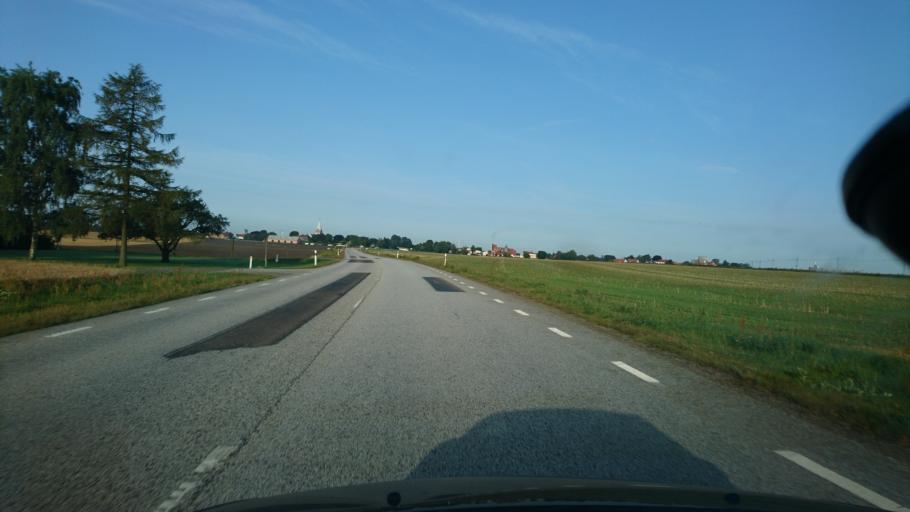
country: SE
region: Skane
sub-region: Simrishamns Kommun
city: Simrishamn
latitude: 55.5355
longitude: 14.2508
